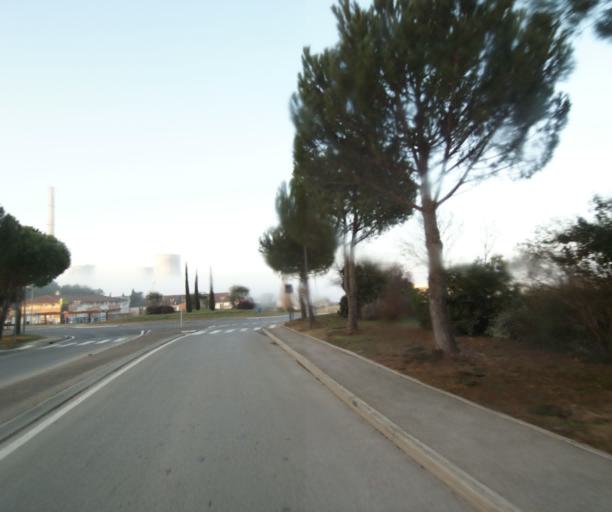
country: FR
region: Provence-Alpes-Cote d'Azur
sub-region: Departement des Bouches-du-Rhone
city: Meyreuil
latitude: 43.4782
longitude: 5.4921
